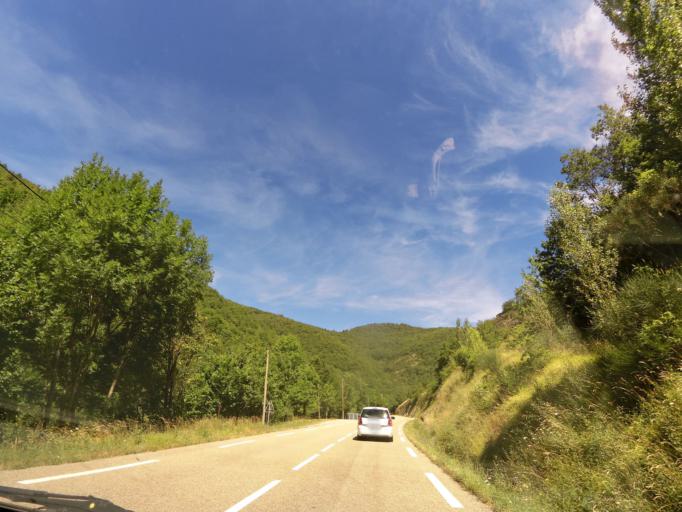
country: FR
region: Languedoc-Roussillon
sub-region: Departement du Gard
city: Le Vigan
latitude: 43.9787
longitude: 3.4696
